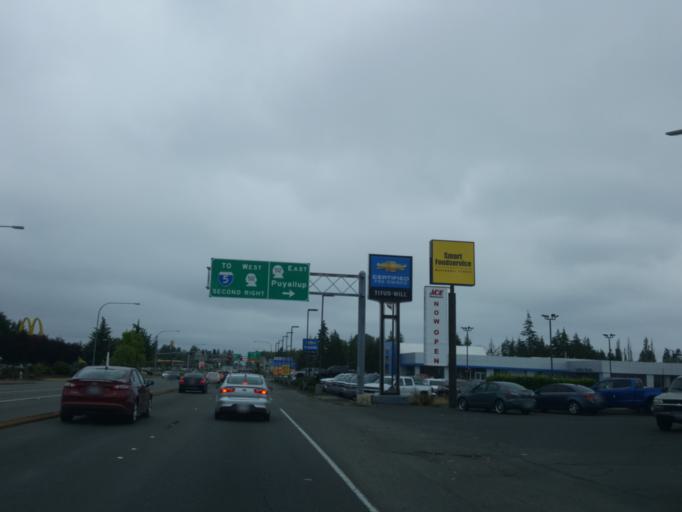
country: US
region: Washington
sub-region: Pierce County
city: Parkland
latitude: 47.1559
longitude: -122.4341
